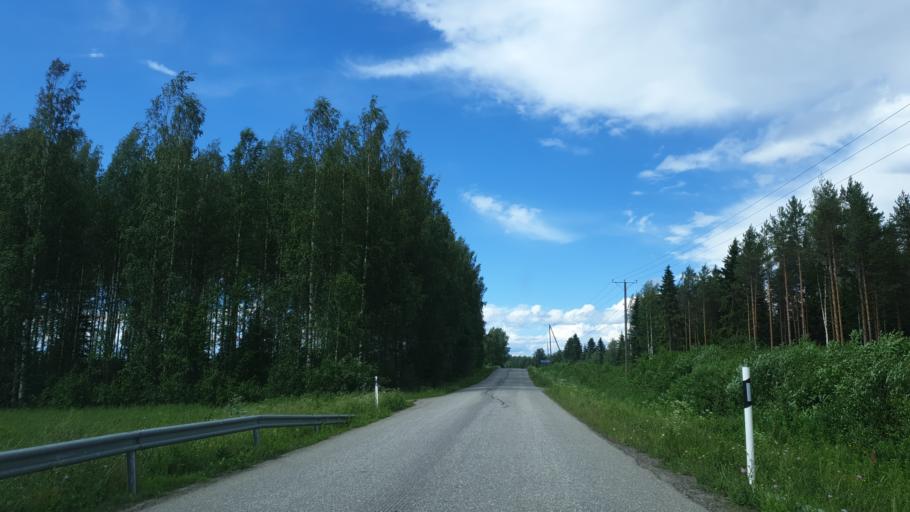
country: FI
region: Northern Savo
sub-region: Koillis-Savo
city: Kaavi
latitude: 62.9866
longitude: 28.7338
